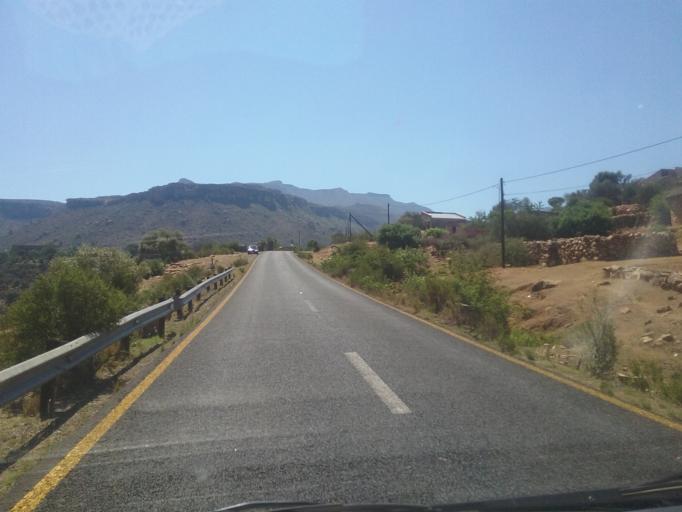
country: LS
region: Quthing
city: Quthing
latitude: -30.3377
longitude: 27.7352
